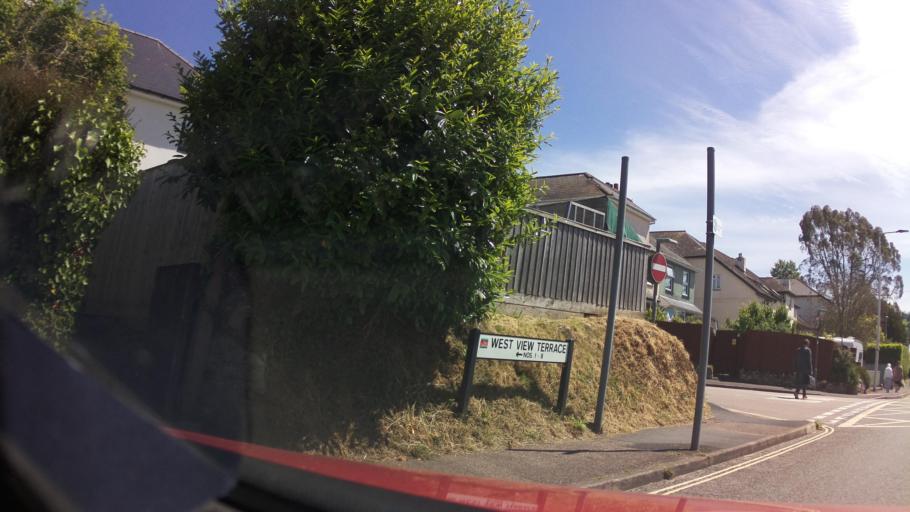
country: GB
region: England
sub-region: Devon
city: Honiton
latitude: 50.8005
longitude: -3.1955
